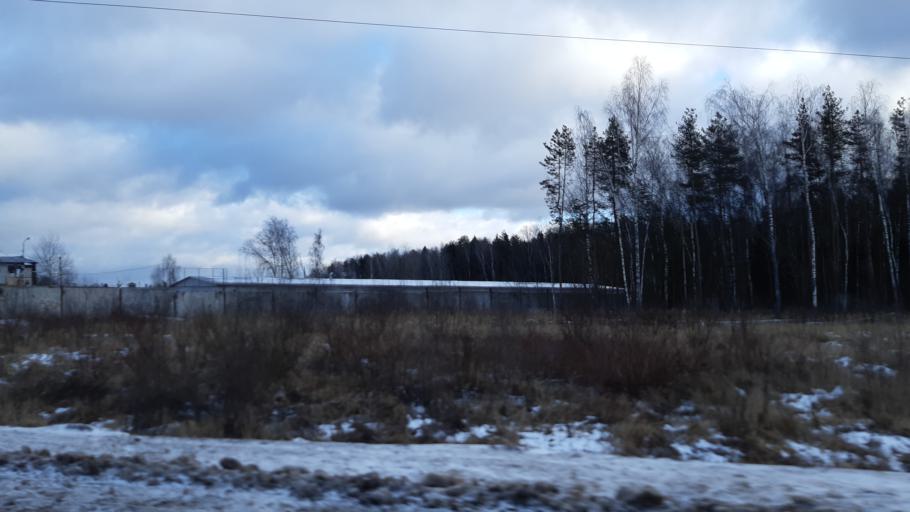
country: RU
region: Moskovskaya
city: Noginsk-9
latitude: 55.9452
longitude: 38.5504
